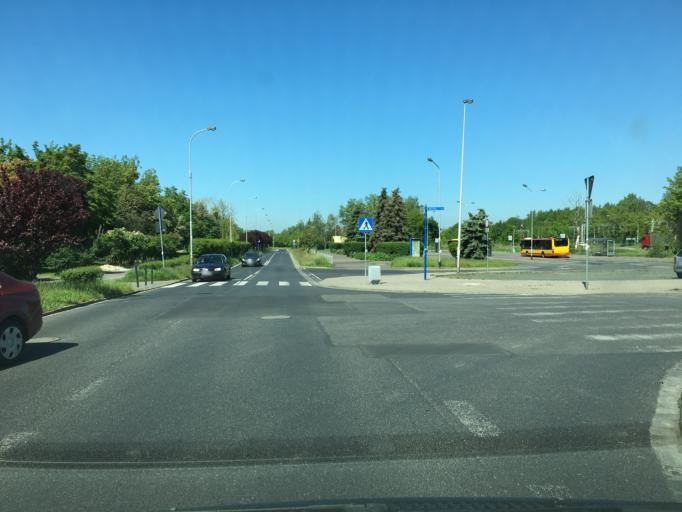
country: PL
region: Lower Silesian Voivodeship
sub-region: Powiat wroclawski
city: Wroclaw
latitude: 51.1188
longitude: 16.9531
